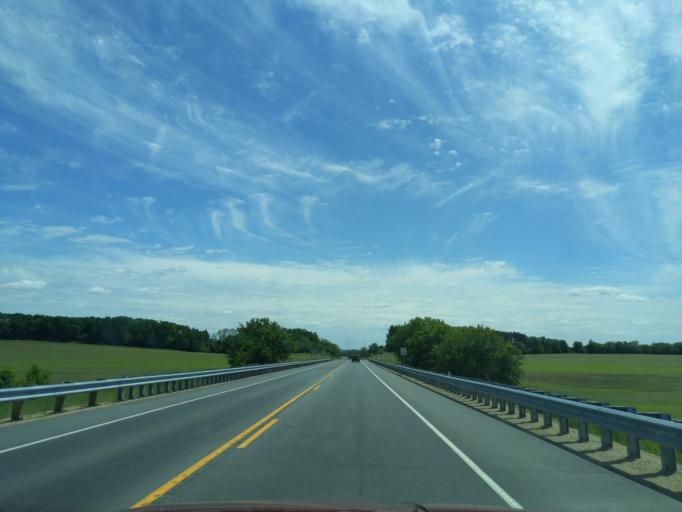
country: US
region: Wisconsin
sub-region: Columbia County
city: Pardeeville
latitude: 43.5692
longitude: -89.3057
